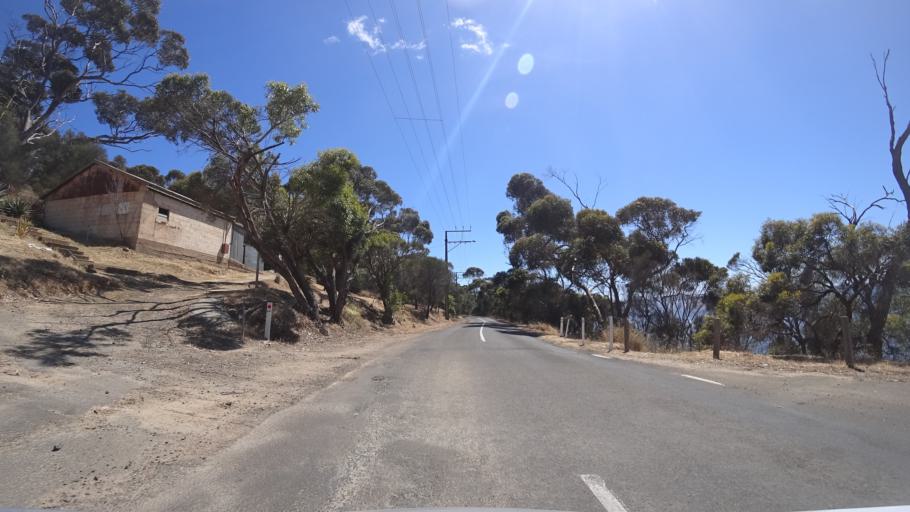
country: AU
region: South Australia
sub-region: Kangaroo Island
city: Kingscote
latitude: -35.7793
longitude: 137.7737
